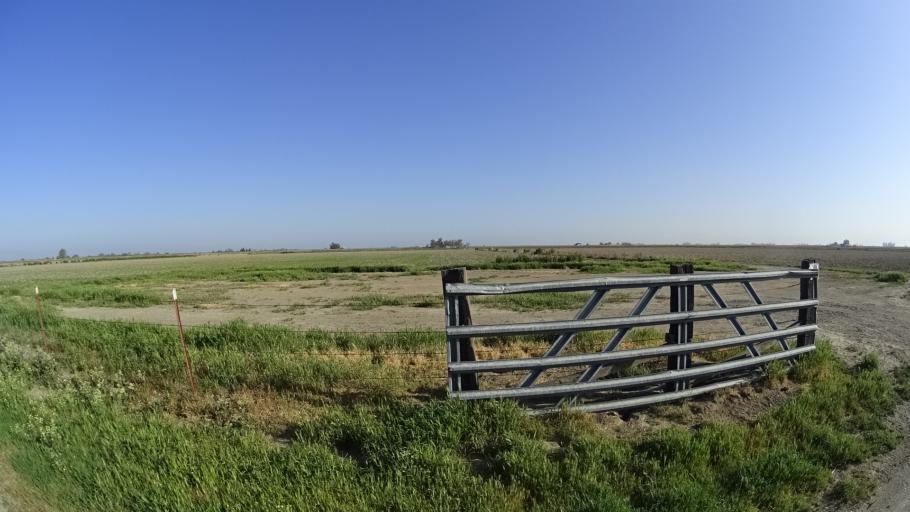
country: US
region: California
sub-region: Glenn County
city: Willows
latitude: 39.5424
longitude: -122.1419
